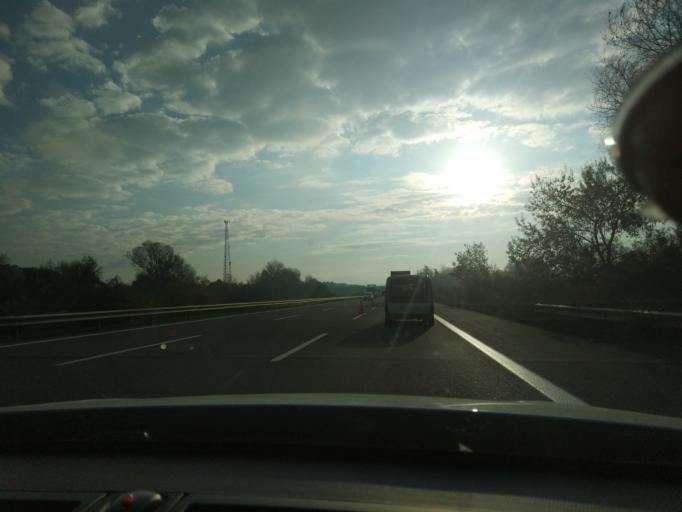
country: TR
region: Duzce
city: Duzce
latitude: 40.8121
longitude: 31.1114
